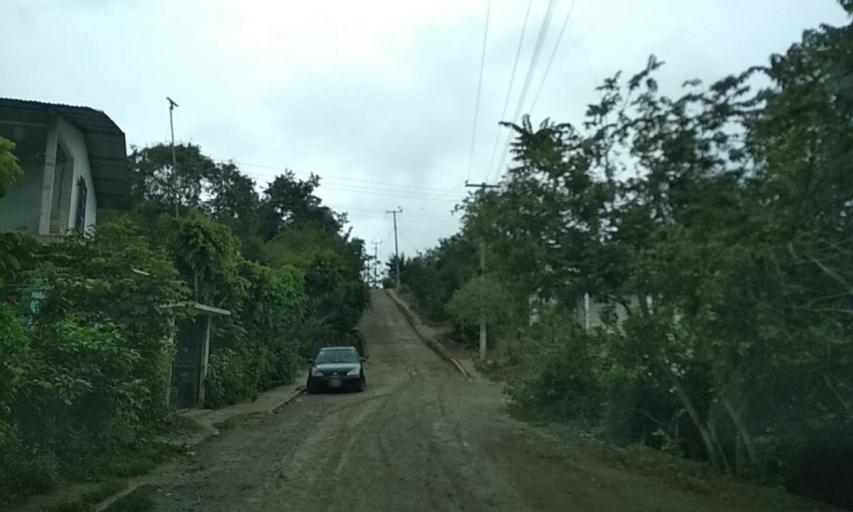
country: MX
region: Veracruz
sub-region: Papantla
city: El Chote
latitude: 20.3837
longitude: -97.3544
